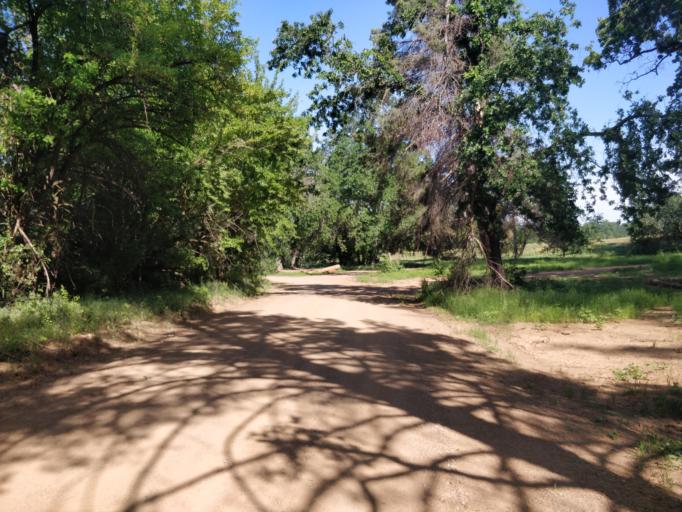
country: US
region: California
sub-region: Shasta County
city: Shasta Lake
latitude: 40.6305
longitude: -122.3117
